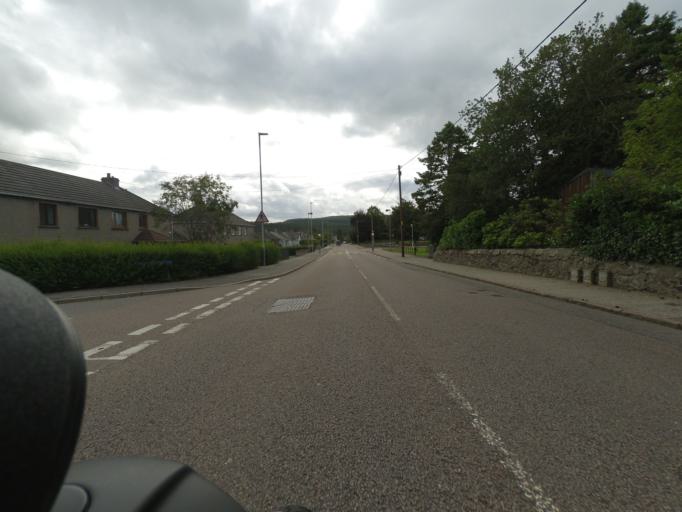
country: GB
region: Scotland
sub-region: Aberdeenshire
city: Banchory
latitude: 57.0542
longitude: -2.4903
